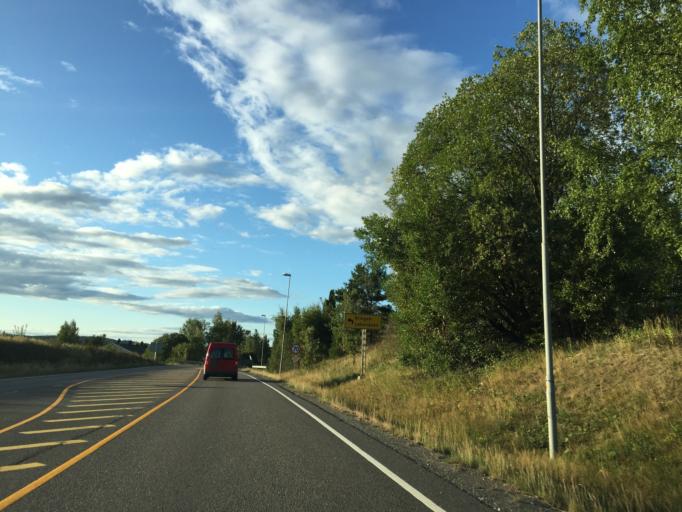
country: NO
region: Akershus
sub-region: Fet
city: Fetsund
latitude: 59.9185
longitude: 11.1839
